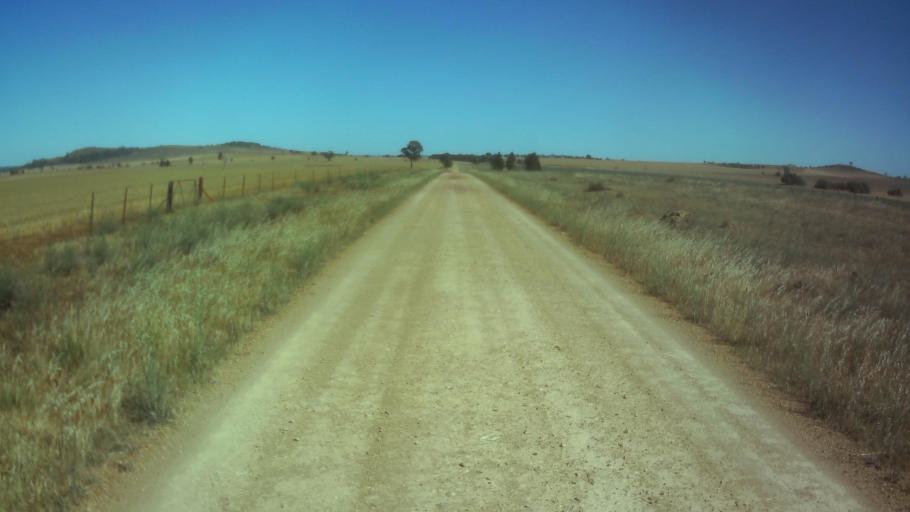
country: AU
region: New South Wales
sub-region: Weddin
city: Grenfell
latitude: -33.9776
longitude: 148.3249
